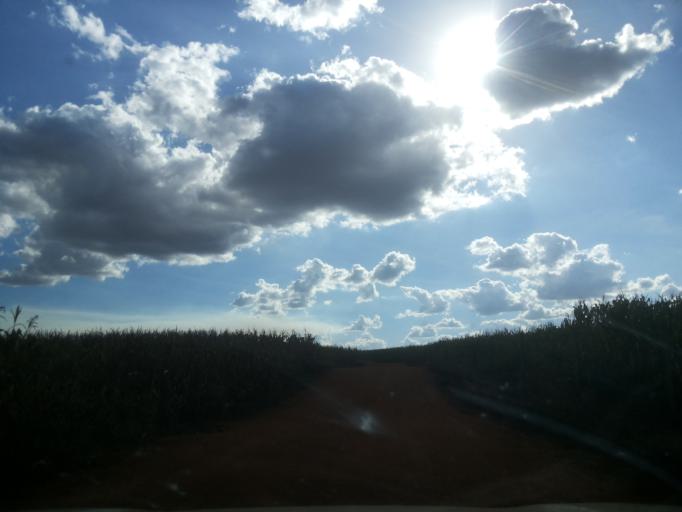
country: BR
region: Minas Gerais
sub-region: Capinopolis
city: Capinopolis
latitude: -18.5827
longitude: -49.4985
